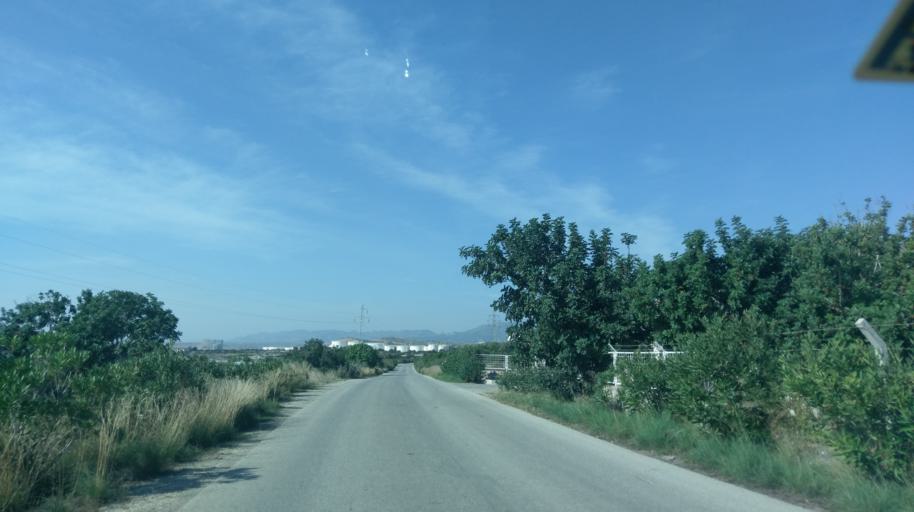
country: CY
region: Ammochostos
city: Trikomo
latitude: 35.3267
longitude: 34.0032
